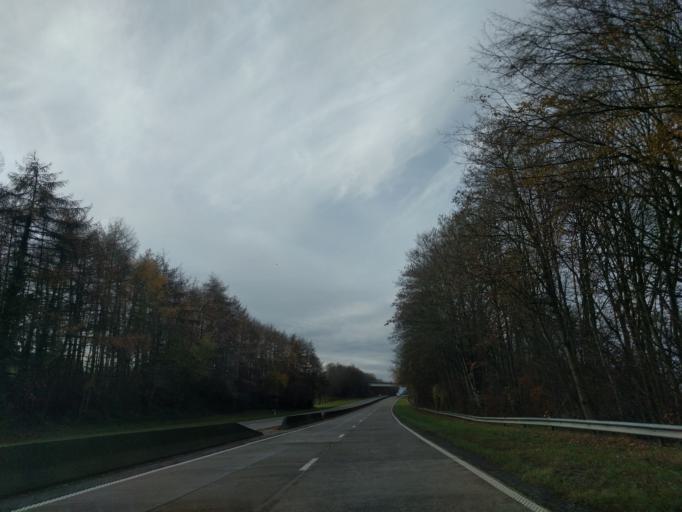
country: BE
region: Wallonia
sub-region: Province de Namur
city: Houyet
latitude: 50.2476
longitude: 5.0086
